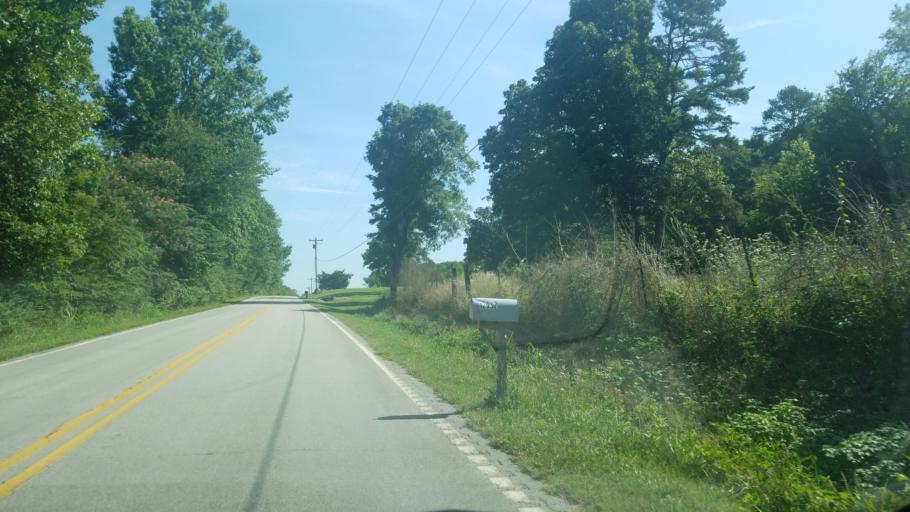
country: US
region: Tennessee
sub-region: Hamilton County
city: Sale Creek
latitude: 35.3033
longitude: -85.0358
